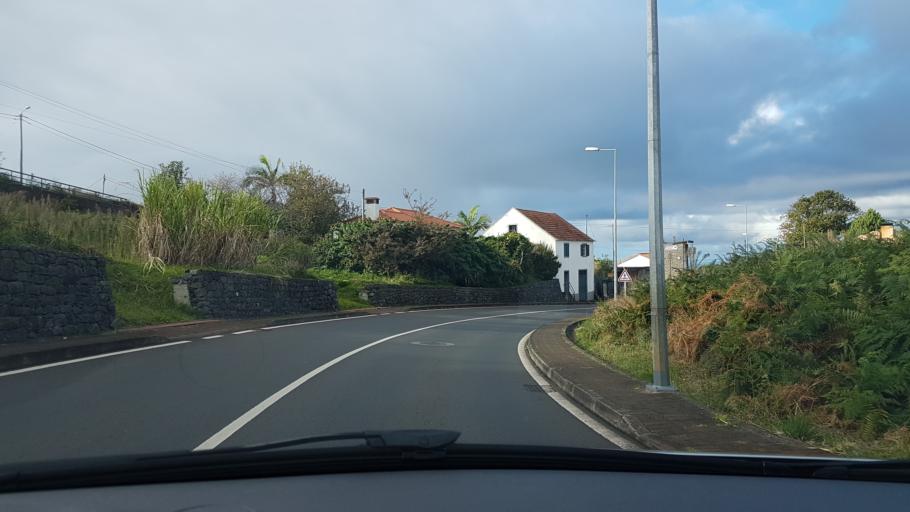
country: PT
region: Madeira
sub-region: Santana
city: Santana
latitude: 32.8140
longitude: -16.8869
